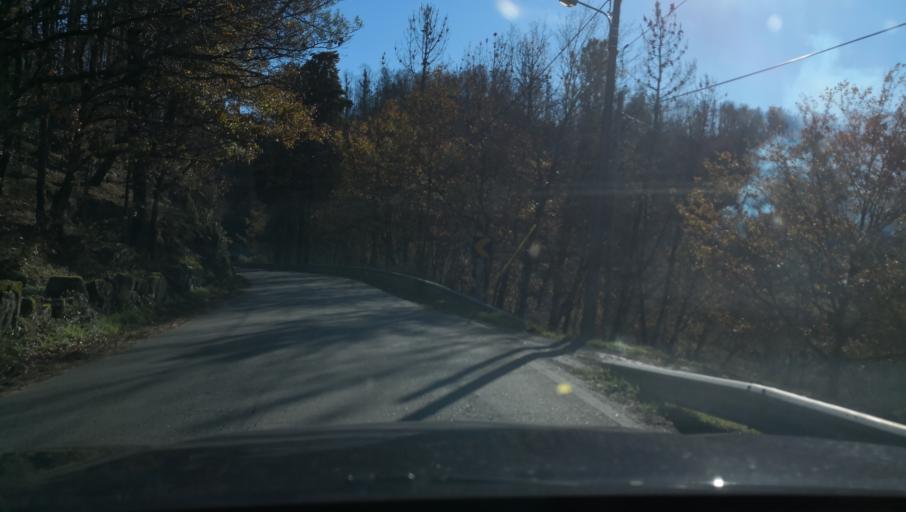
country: PT
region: Viseu
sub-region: Oliveira de Frades
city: Oliveira de Frades
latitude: 40.7304
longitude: -8.1510
